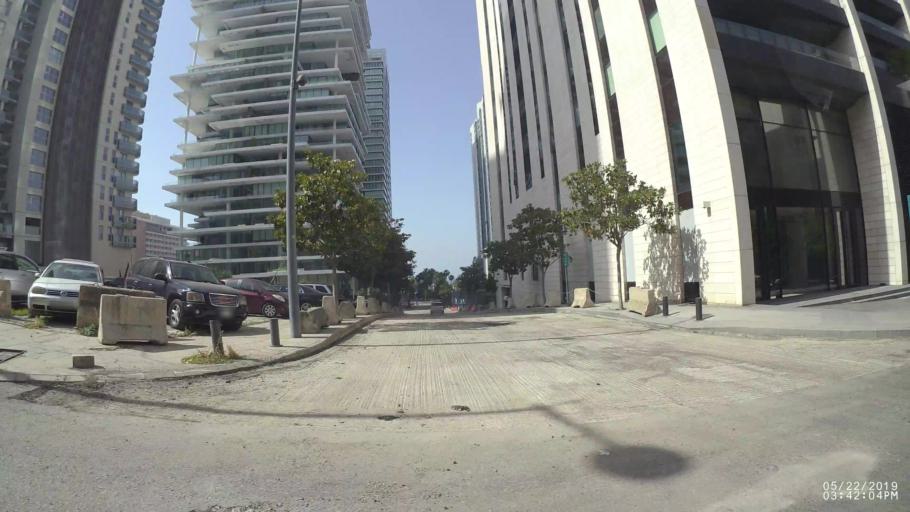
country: LB
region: Beyrouth
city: Beirut
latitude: 33.8988
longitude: 35.4969
